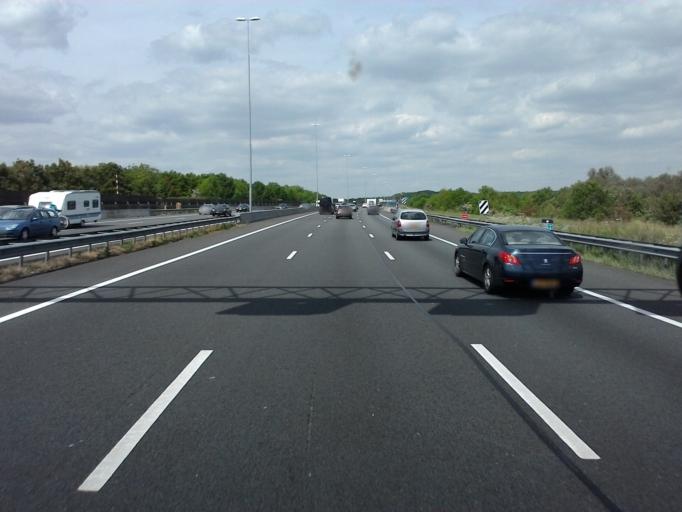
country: NL
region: Gelderland
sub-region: Gemeente Overbetuwe
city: Heteren
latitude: 51.9579
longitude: 5.7647
